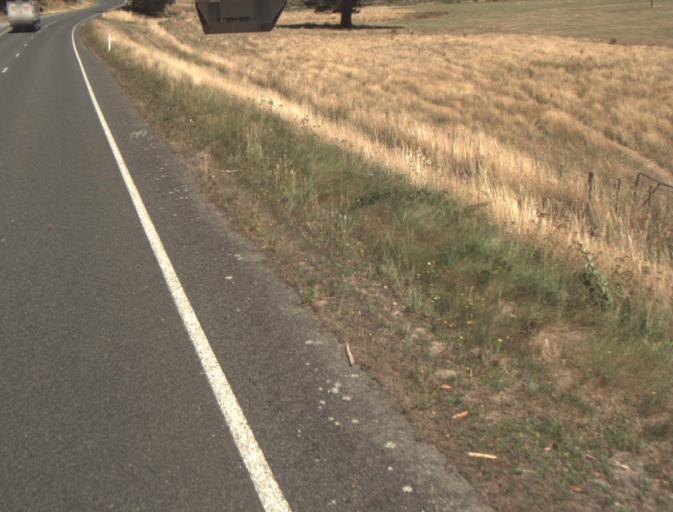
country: AU
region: Tasmania
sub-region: Dorset
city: Scottsdale
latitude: -41.3176
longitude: 147.3657
